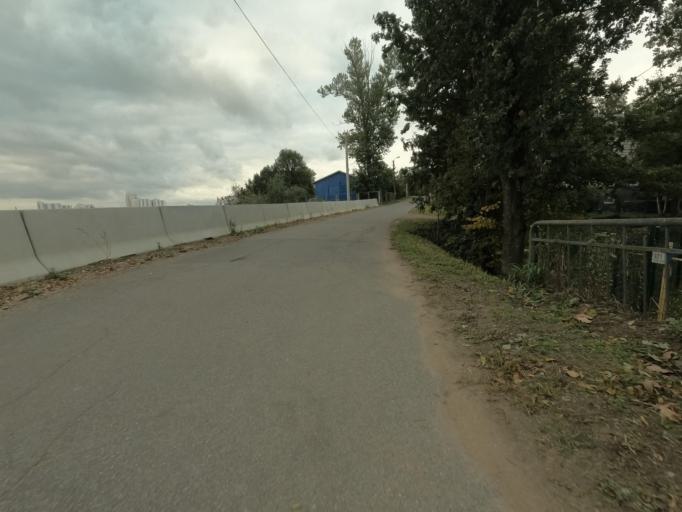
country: RU
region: St.-Petersburg
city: Pontonnyy
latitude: 59.8025
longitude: 30.6085
